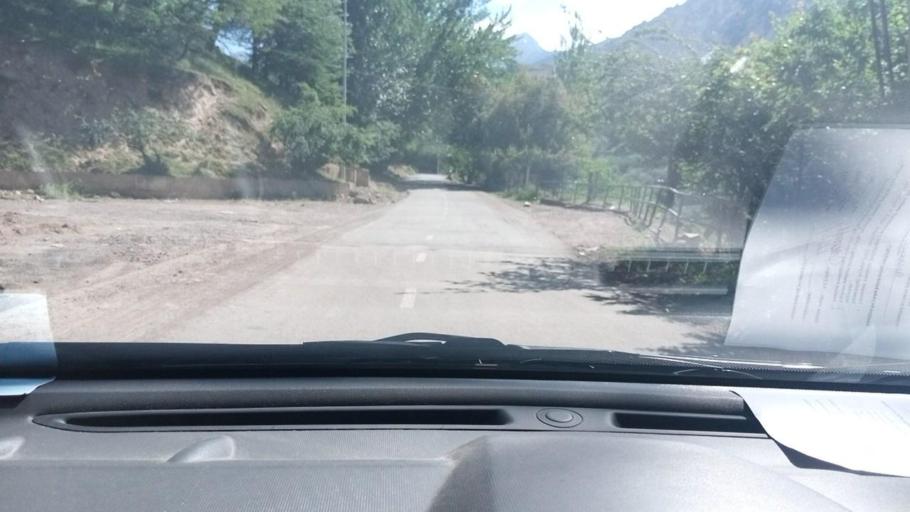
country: UZ
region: Toshkent
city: Yangiobod
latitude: 41.1223
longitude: 70.1021
